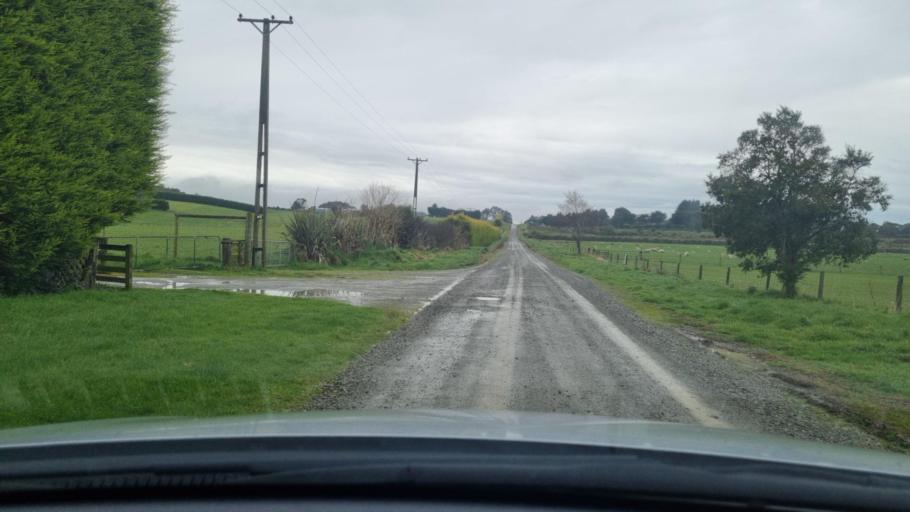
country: NZ
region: Southland
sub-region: Invercargill City
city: Invercargill
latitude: -46.3222
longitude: 168.3331
